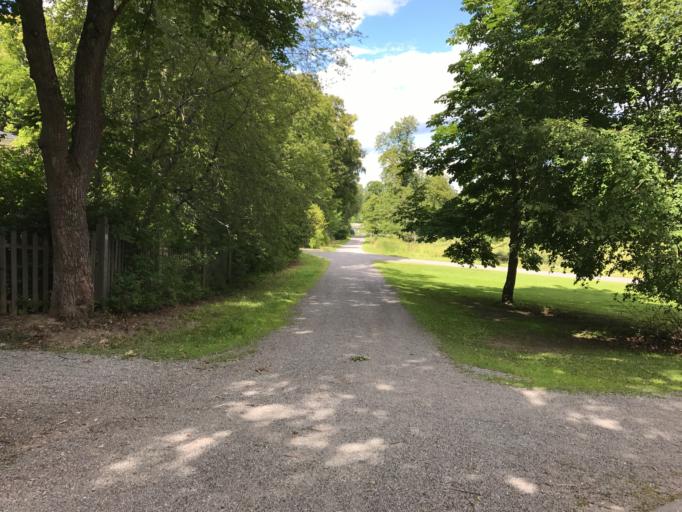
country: SE
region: Stockholm
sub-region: Stockholms Kommun
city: OEstermalm
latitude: 59.3281
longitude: 18.1188
